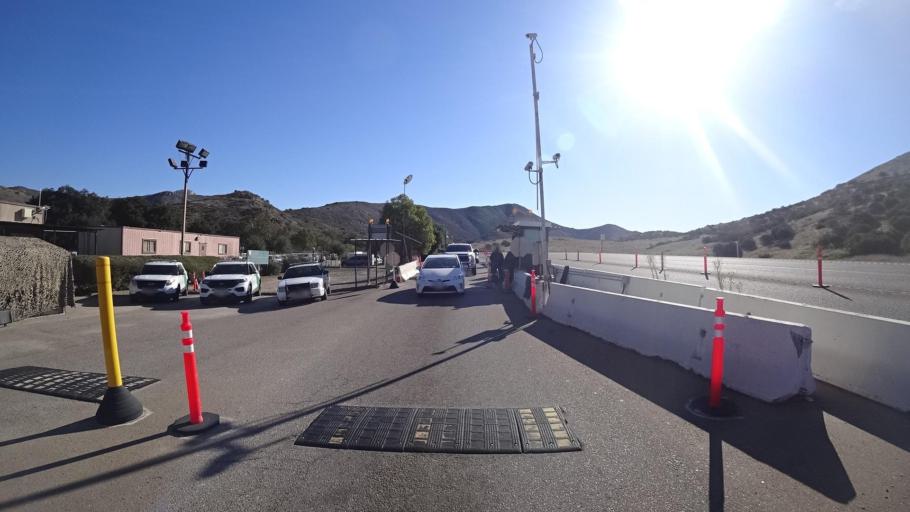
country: US
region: California
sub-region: San Diego County
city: Jamul
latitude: 32.6641
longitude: -116.8187
